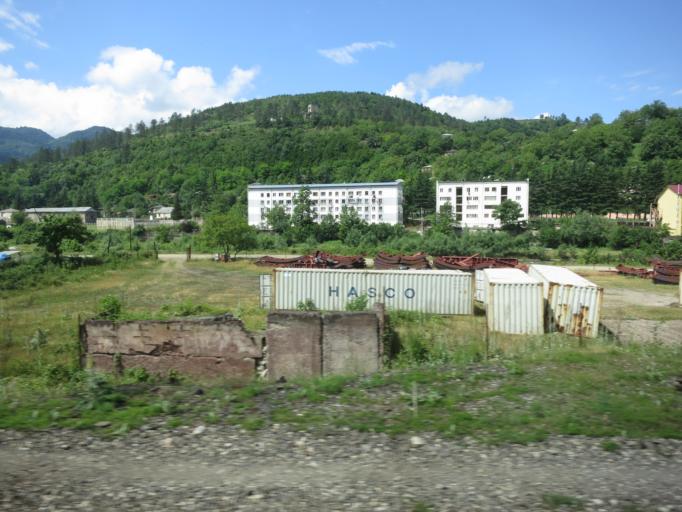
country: GE
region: Imereti
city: Kharagauli
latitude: 42.0179
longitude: 43.2049
